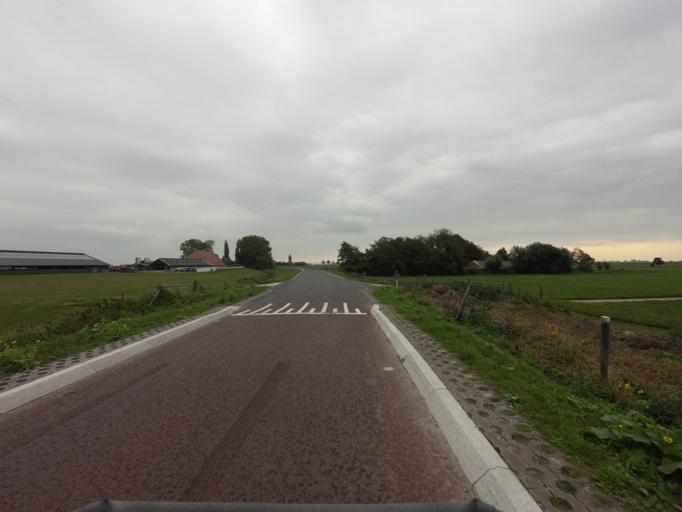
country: NL
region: Friesland
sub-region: Sudwest Fryslan
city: Bolsward
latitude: 53.0186
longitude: 5.5425
